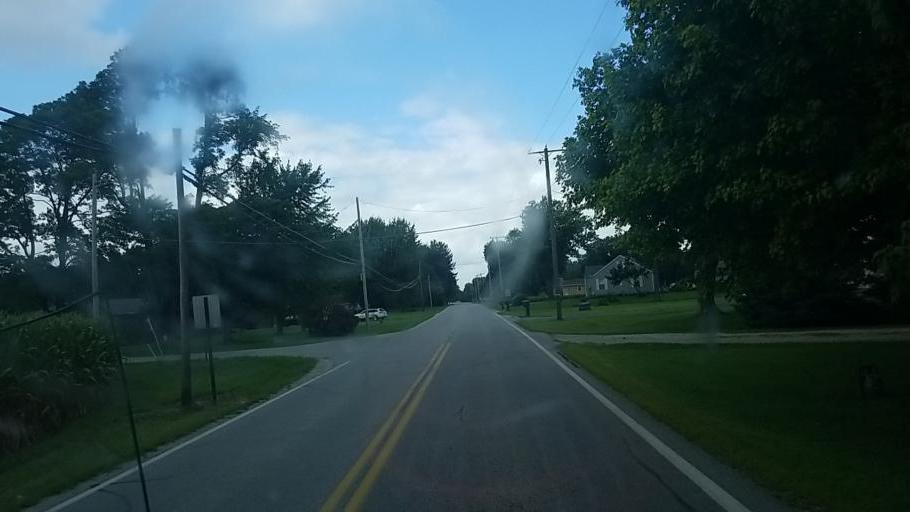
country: US
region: Ohio
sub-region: Clark County
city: Springfield
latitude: 39.8816
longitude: -83.7802
